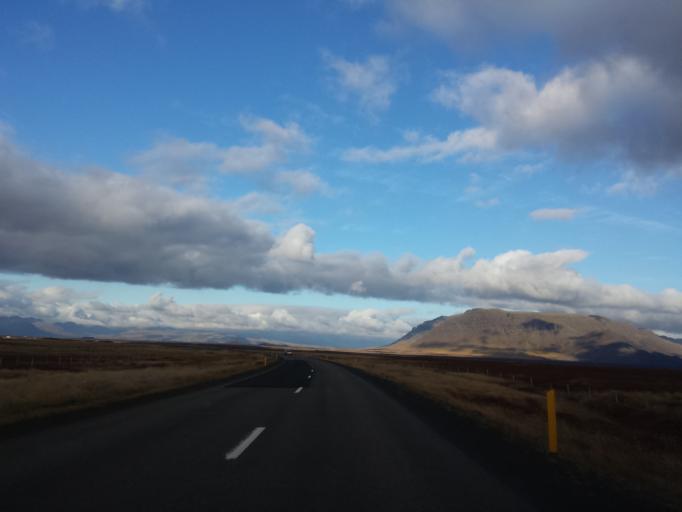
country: IS
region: West
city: Borgarnes
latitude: 64.7104
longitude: -22.1473
